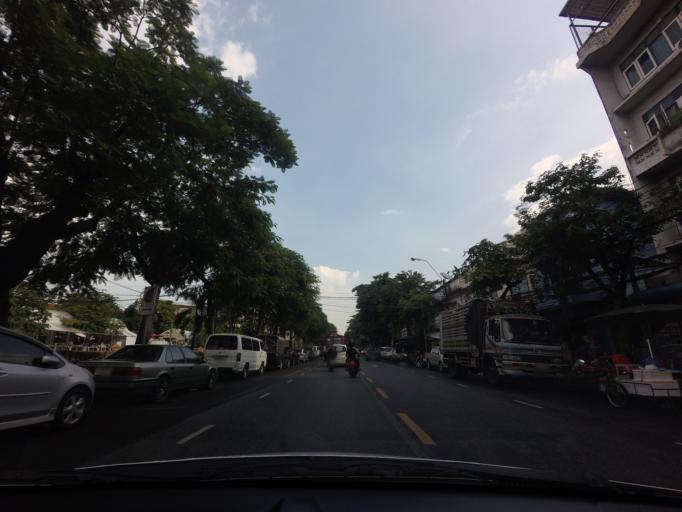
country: TH
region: Bangkok
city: Pom Prap Sattru Phai
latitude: 13.7627
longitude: 100.5101
